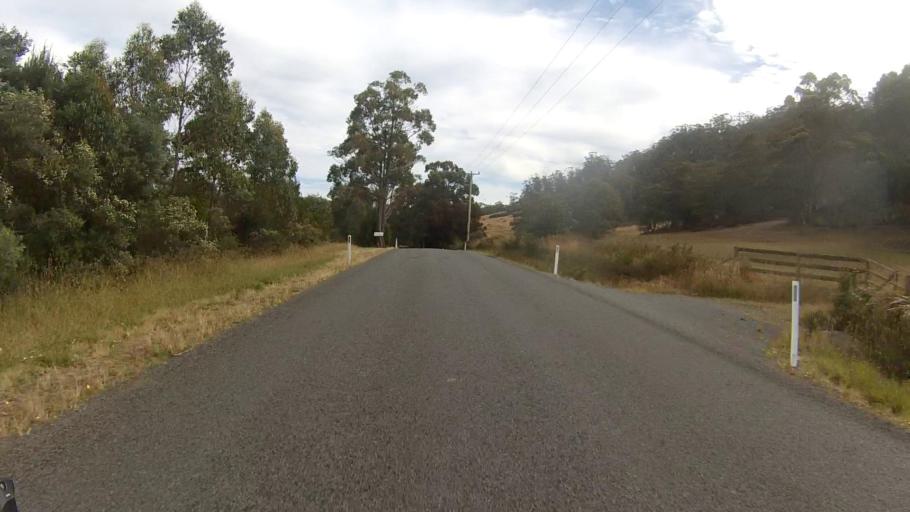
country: AU
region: Tasmania
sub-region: Sorell
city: Sorell
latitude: -42.8092
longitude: 147.7945
